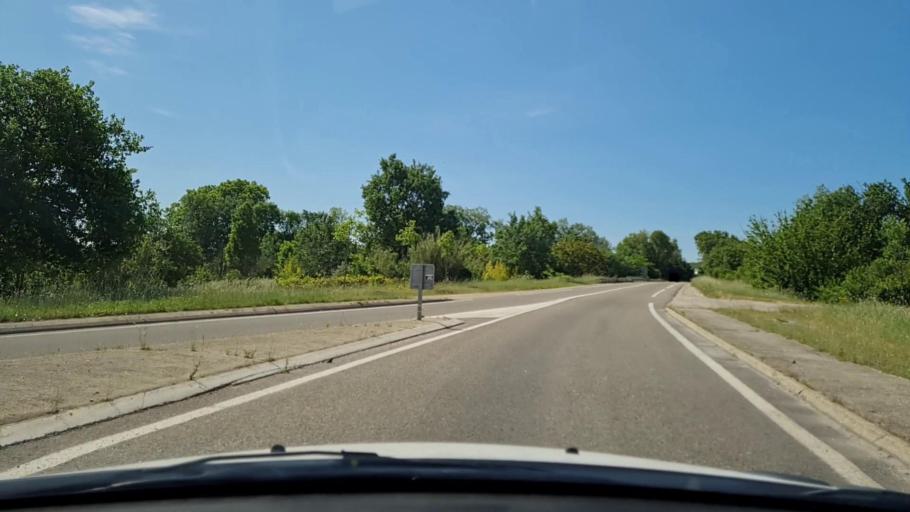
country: FR
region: Languedoc-Roussillon
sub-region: Departement du Gard
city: La Calmette
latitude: 43.9327
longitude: 4.2565
